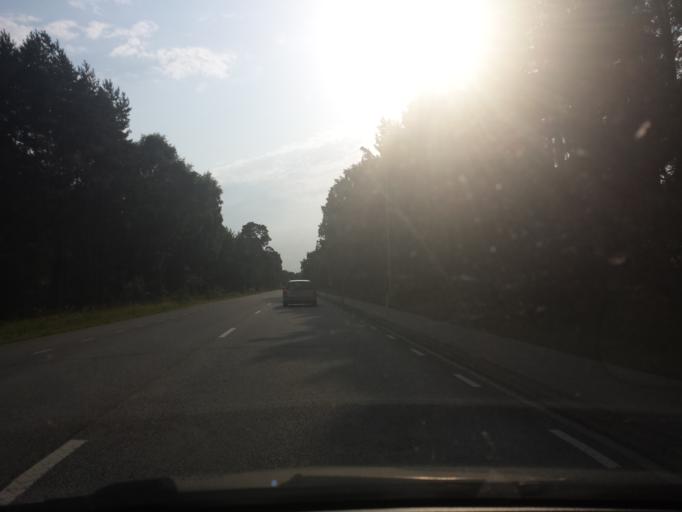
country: SE
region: Skane
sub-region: Ystads Kommun
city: Ystad
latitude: 55.4338
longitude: 13.8728
